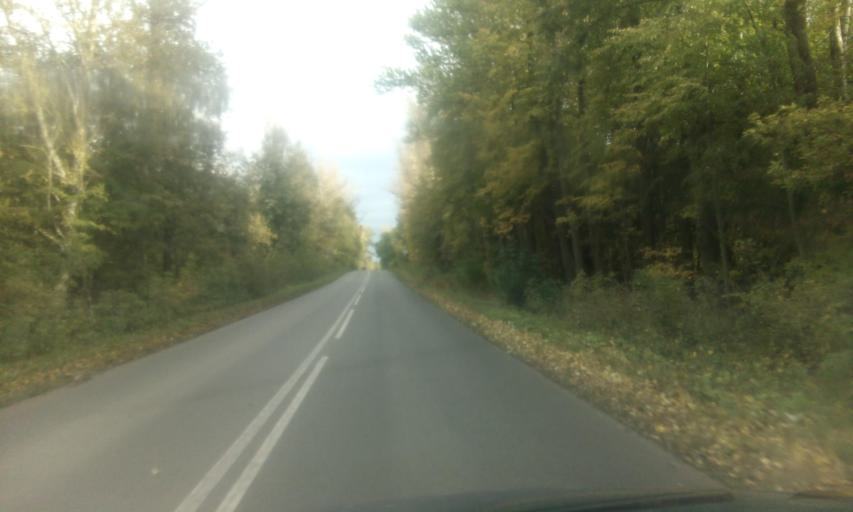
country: RU
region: Tula
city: Partizan
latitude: 53.9609
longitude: 38.0875
